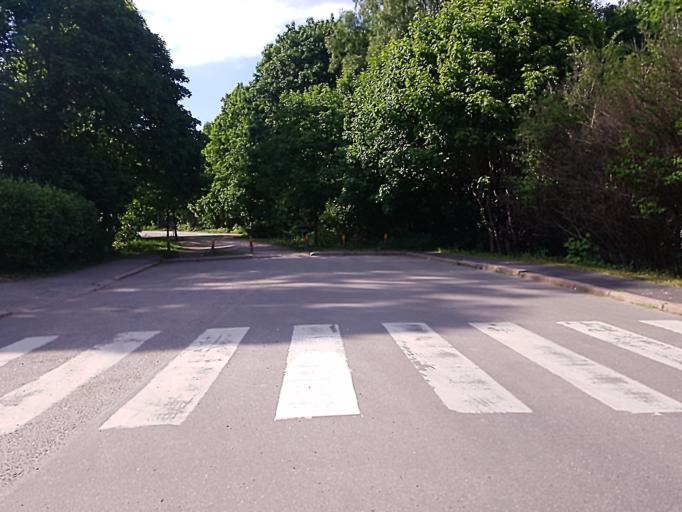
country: FI
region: Uusimaa
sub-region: Helsinki
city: Helsinki
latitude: 60.2389
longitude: 24.9695
